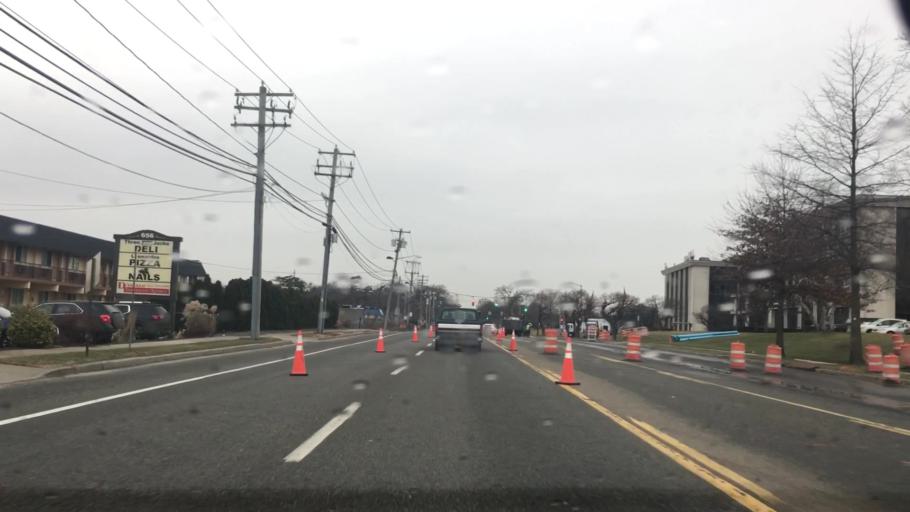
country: US
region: New York
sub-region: Suffolk County
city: Brentwood
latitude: 40.8075
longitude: -73.2448
